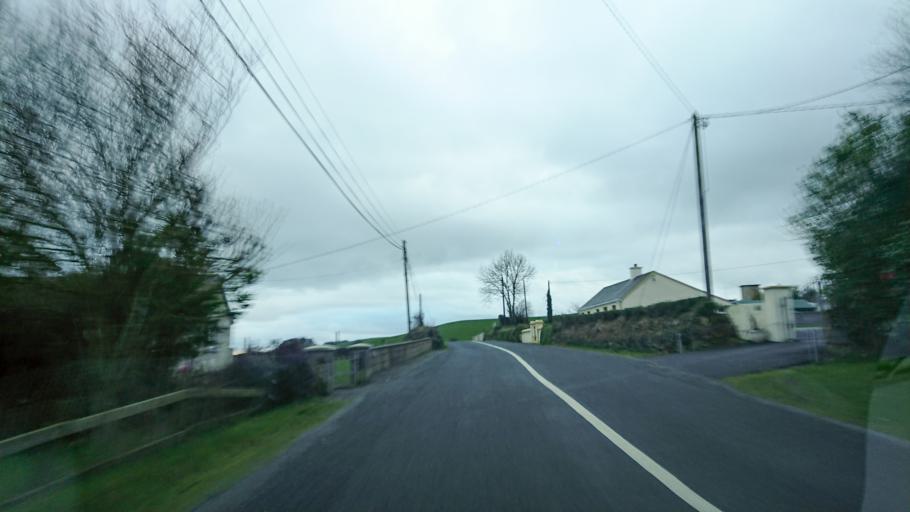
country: IE
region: Munster
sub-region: Waterford
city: Portlaw
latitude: 52.1555
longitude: -7.3832
